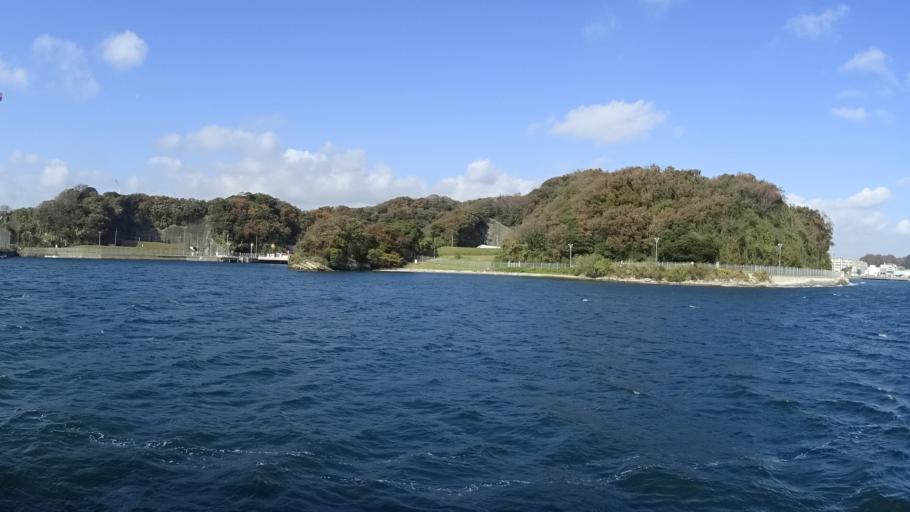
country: JP
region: Kanagawa
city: Yokosuka
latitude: 35.3020
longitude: 139.6425
